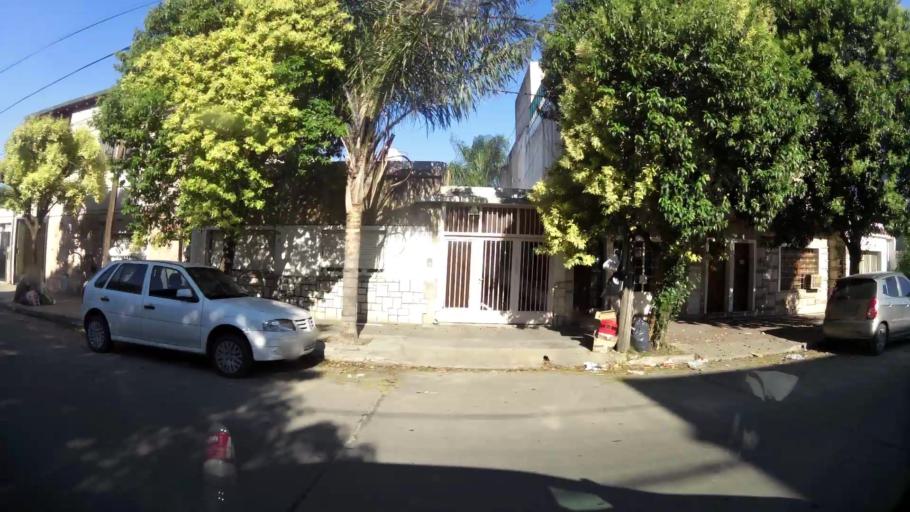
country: AR
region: Cordoba
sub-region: Departamento de Capital
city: Cordoba
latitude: -31.3882
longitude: -64.1784
